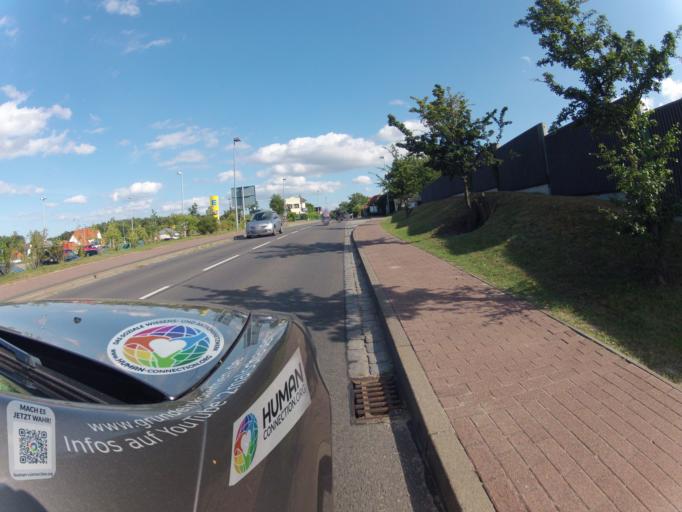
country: DE
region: Mecklenburg-Vorpommern
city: Loddin
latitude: 54.0143
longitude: 14.0474
